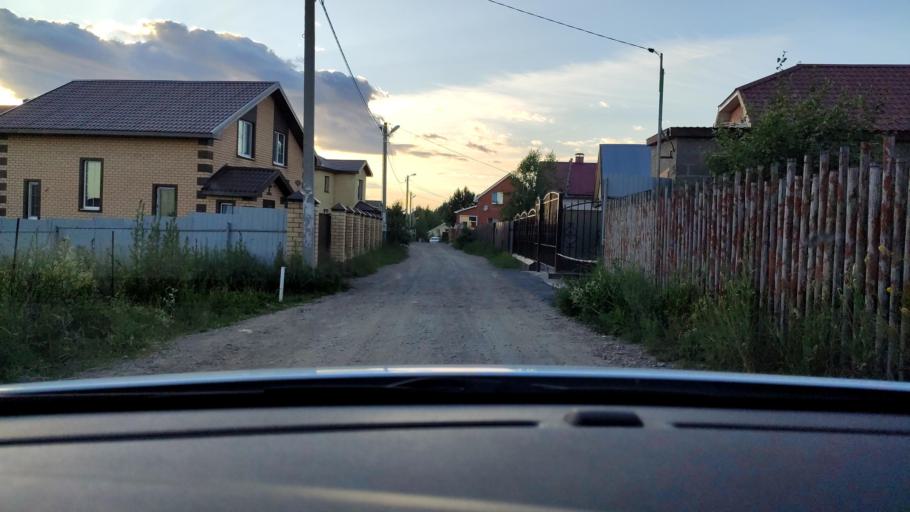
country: RU
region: Tatarstan
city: Stolbishchi
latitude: 55.7601
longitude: 49.3025
